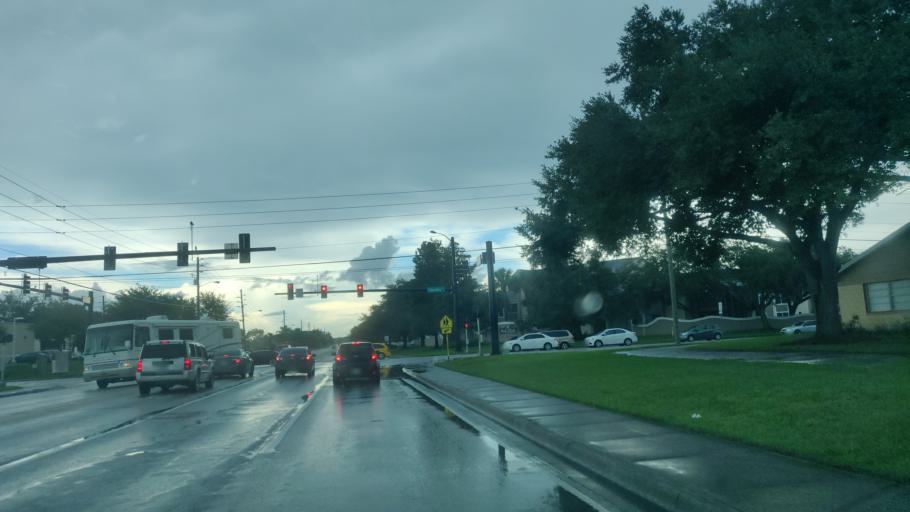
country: US
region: Florida
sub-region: Osceola County
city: Kissimmee
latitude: 28.3076
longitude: -81.4242
